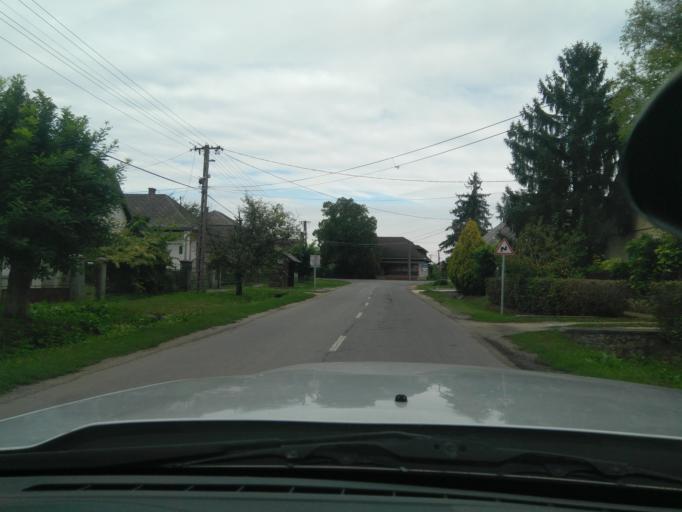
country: HU
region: Fejer
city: Val
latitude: 47.3704
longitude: 18.7417
